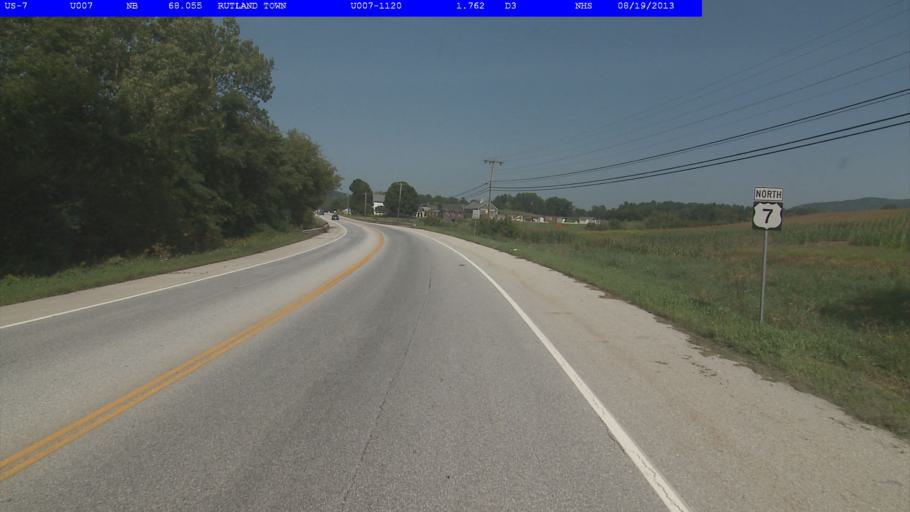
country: US
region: Vermont
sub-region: Rutland County
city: Rutland
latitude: 43.6386
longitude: -72.9763
